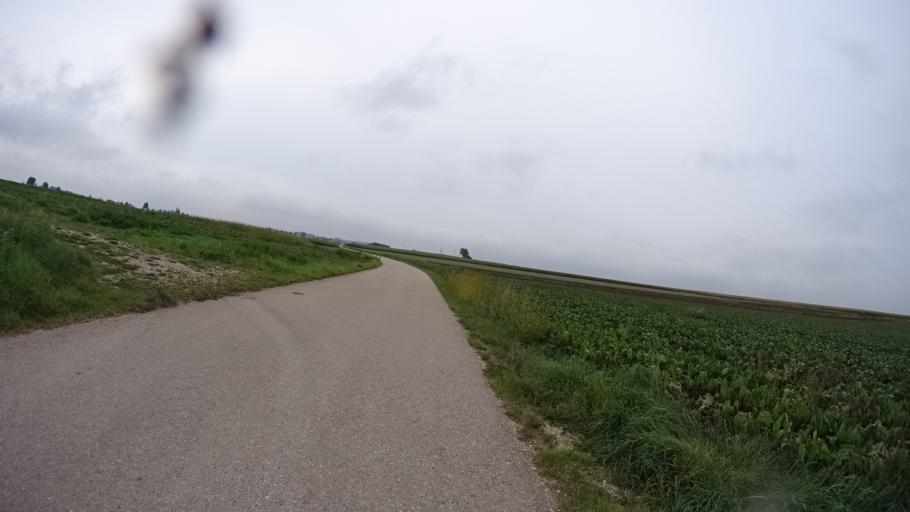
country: DE
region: Bavaria
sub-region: Upper Bavaria
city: Gaimersheim
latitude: 48.8250
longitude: 11.3620
